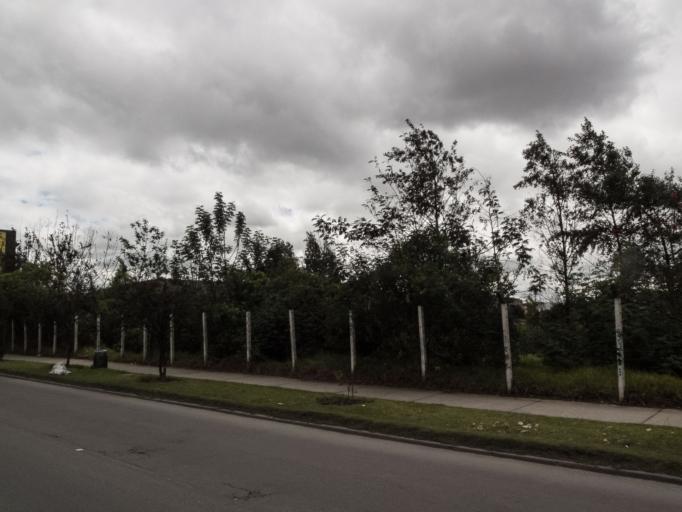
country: CO
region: Bogota D.C.
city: Bogota
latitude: 4.6755
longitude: -74.1281
